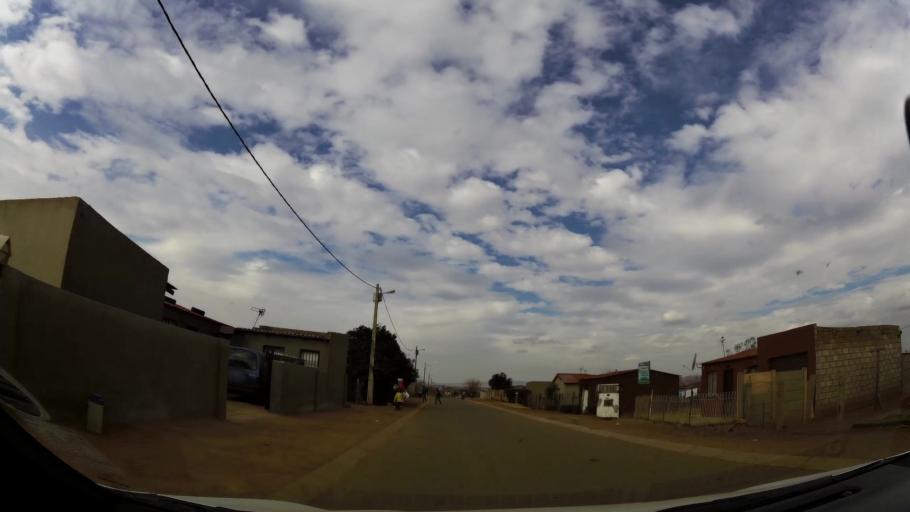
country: ZA
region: Gauteng
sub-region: Ekurhuleni Metropolitan Municipality
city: Germiston
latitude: -26.4034
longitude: 28.1425
